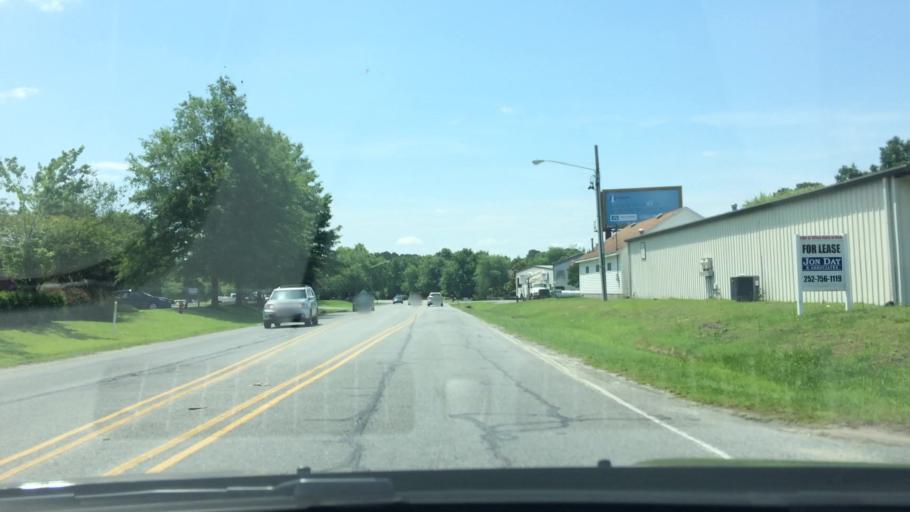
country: US
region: North Carolina
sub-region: Pitt County
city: Windsor
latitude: 35.5626
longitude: -77.3554
